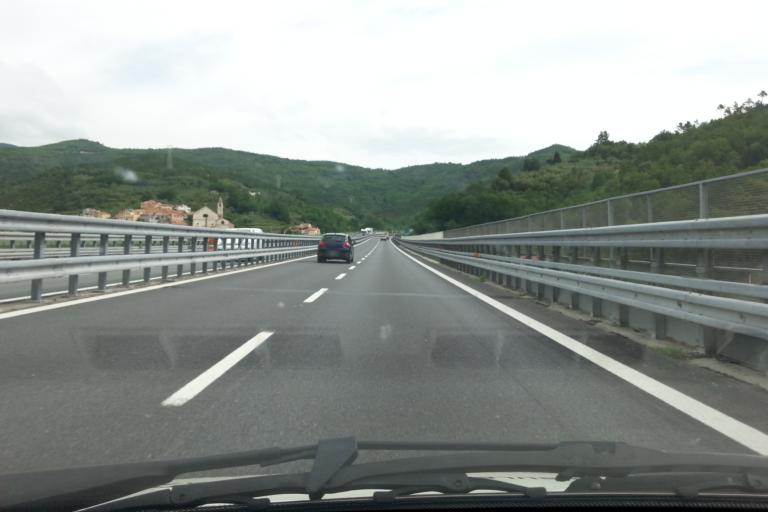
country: IT
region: Liguria
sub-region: Provincia di Savona
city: Feglino
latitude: 44.2168
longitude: 8.3241
